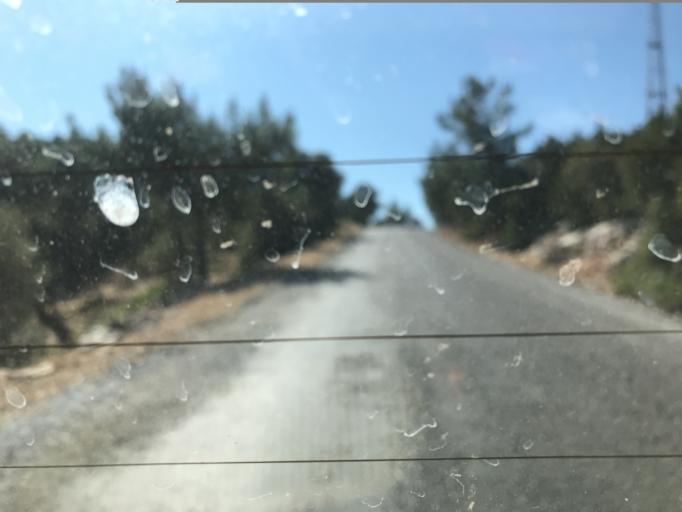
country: TR
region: Mugla
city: Selimiye
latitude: 37.3871
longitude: 27.4821
